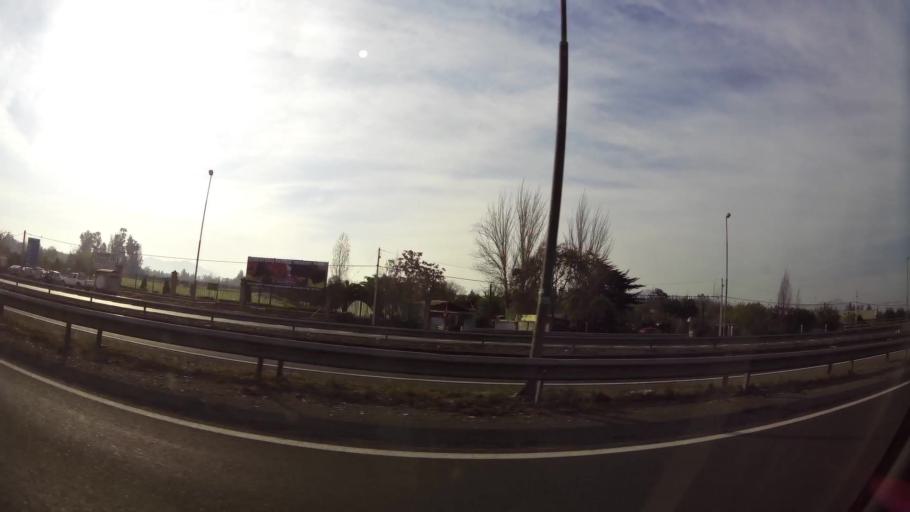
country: CL
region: Santiago Metropolitan
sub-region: Provincia de Talagante
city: Penaflor
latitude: -33.6085
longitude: -70.8514
